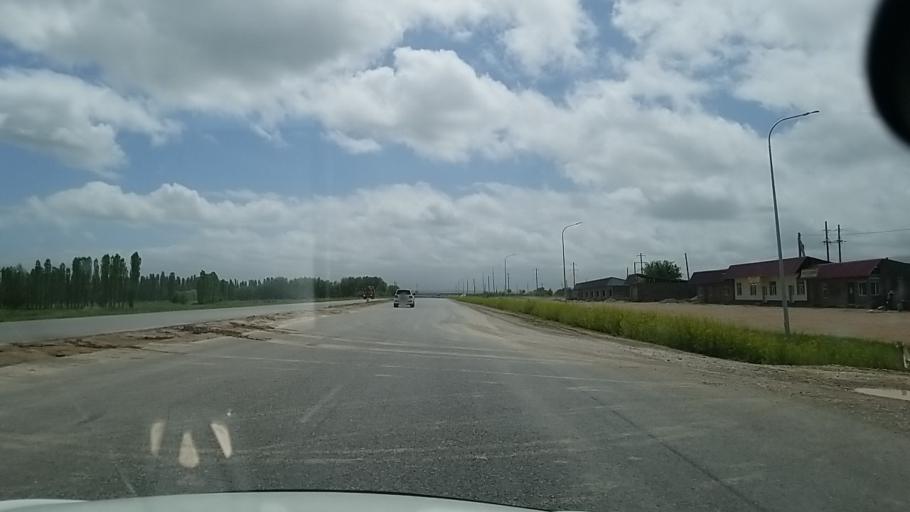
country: KZ
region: Ongtustik Qazaqstan
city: Turar Ryskulov
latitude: 42.5260
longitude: 70.3093
